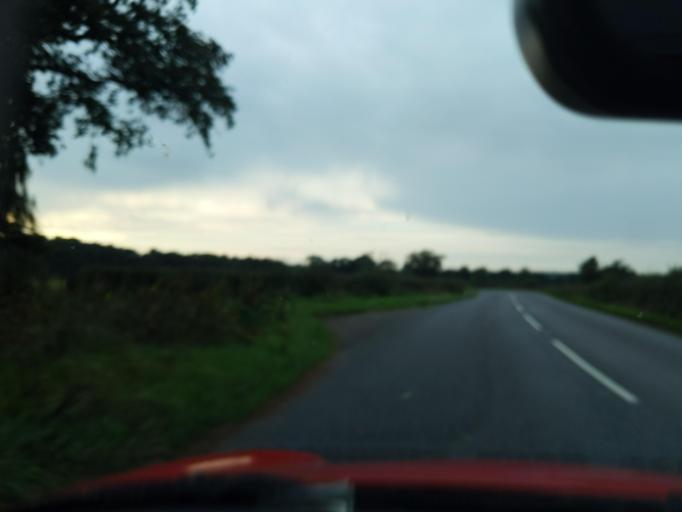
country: GB
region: England
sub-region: Devon
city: Okehampton
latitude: 50.8115
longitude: -4.0613
